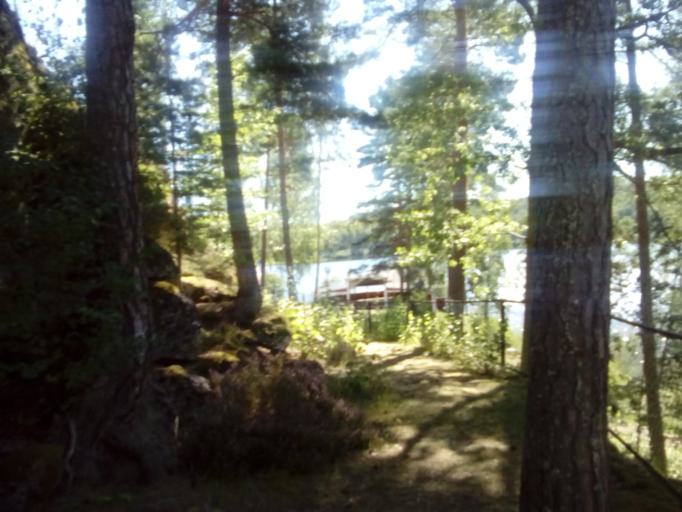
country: SE
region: OEstergoetland
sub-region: Atvidabergs Kommun
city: Atvidaberg
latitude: 58.0148
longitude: 15.9228
